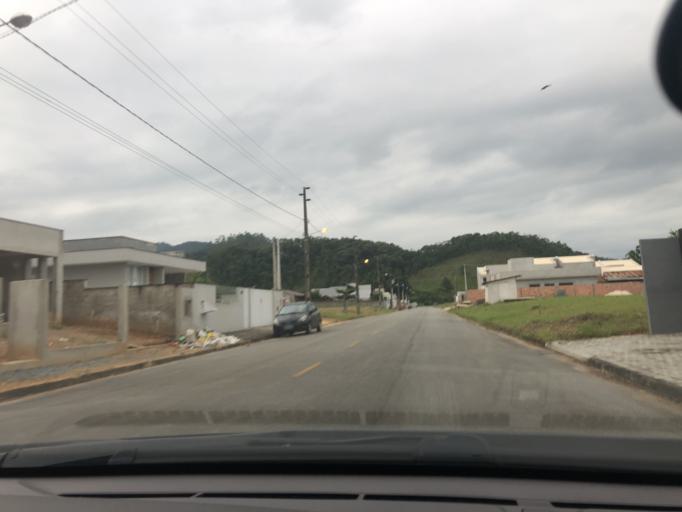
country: BR
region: Santa Catarina
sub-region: Jaragua Do Sul
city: Jaragua do Sul
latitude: -26.5016
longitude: -49.1401
